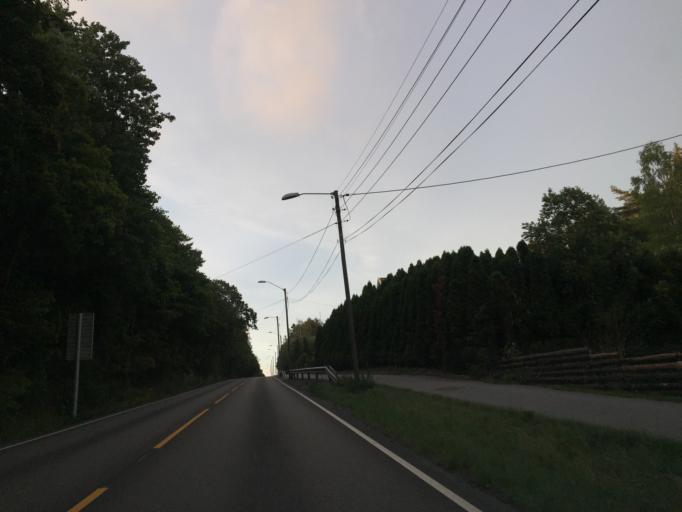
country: NO
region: Ostfold
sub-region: Fredrikstad
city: Fredrikstad
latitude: 59.1841
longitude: 10.9276
